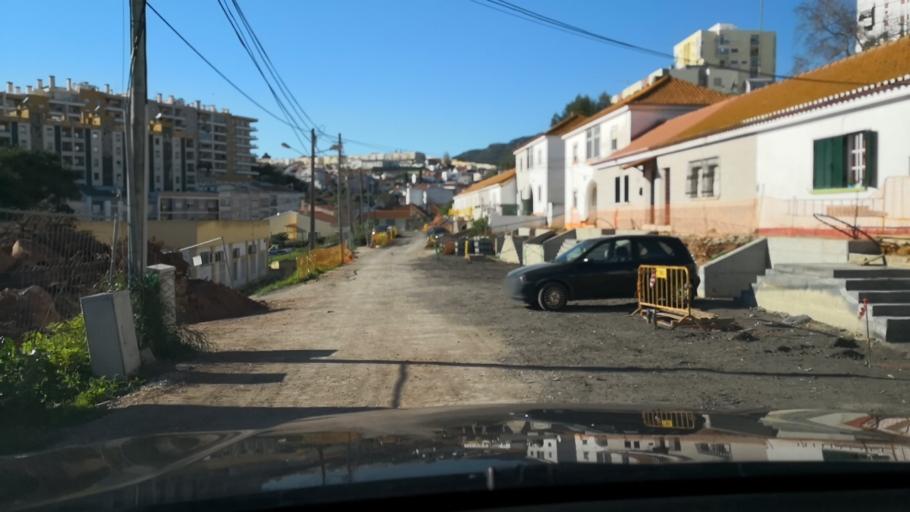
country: PT
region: Setubal
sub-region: Setubal
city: Setubal
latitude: 38.5254
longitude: -8.9049
